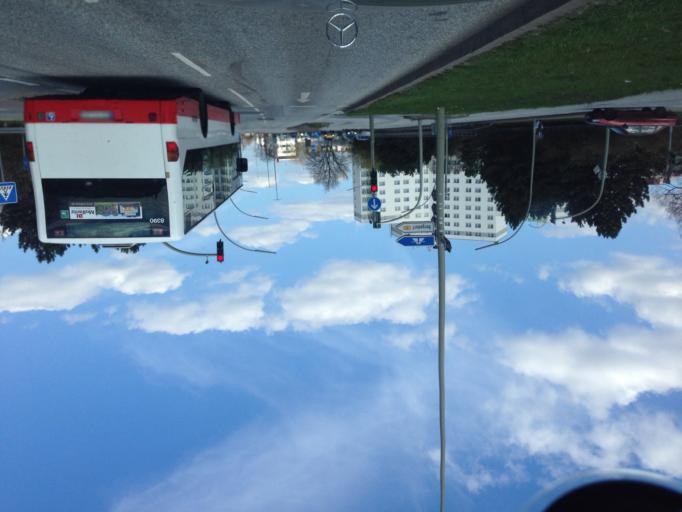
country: DE
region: Hamburg
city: Wandsbek
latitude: 53.5382
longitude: 10.0992
